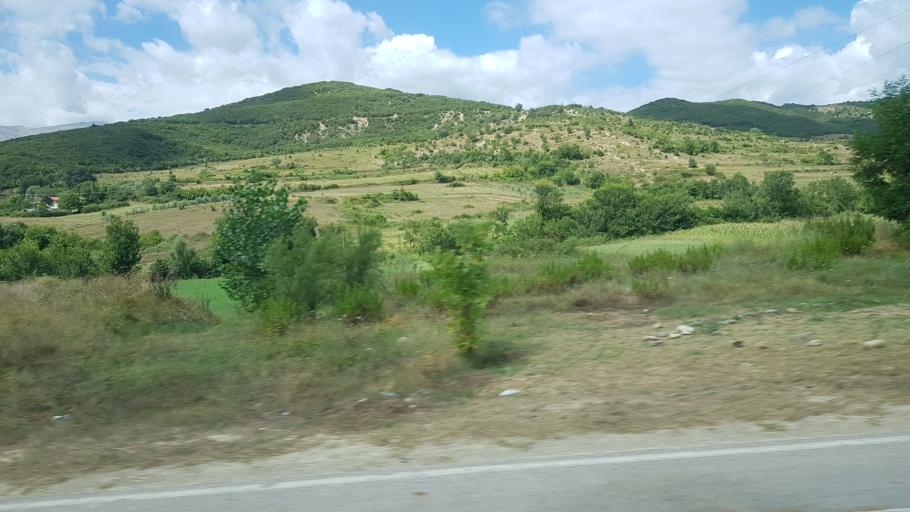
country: AL
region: Gjirokaster
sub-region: Rrethi i Tepelenes
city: Krahes
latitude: 40.4162
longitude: 19.8577
